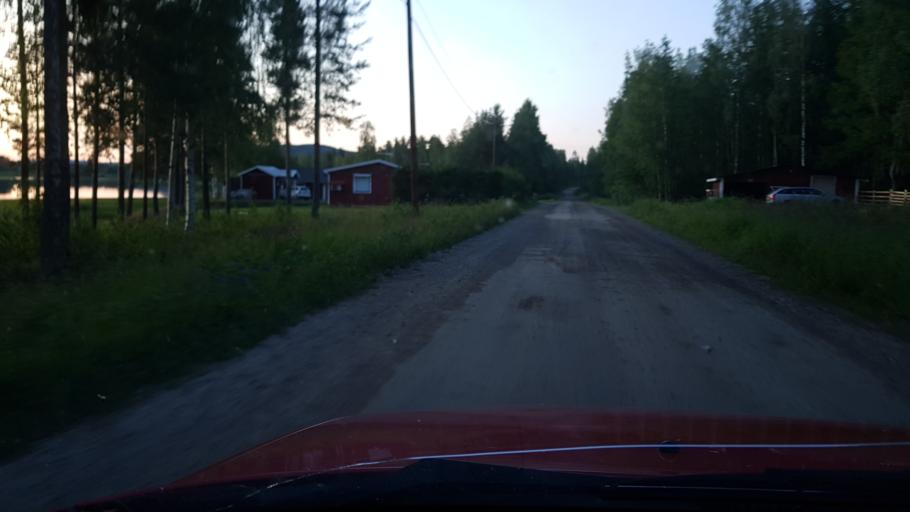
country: SE
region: Norrbotten
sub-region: Alvsbyns Kommun
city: AElvsbyn
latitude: 65.7010
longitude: 20.6803
